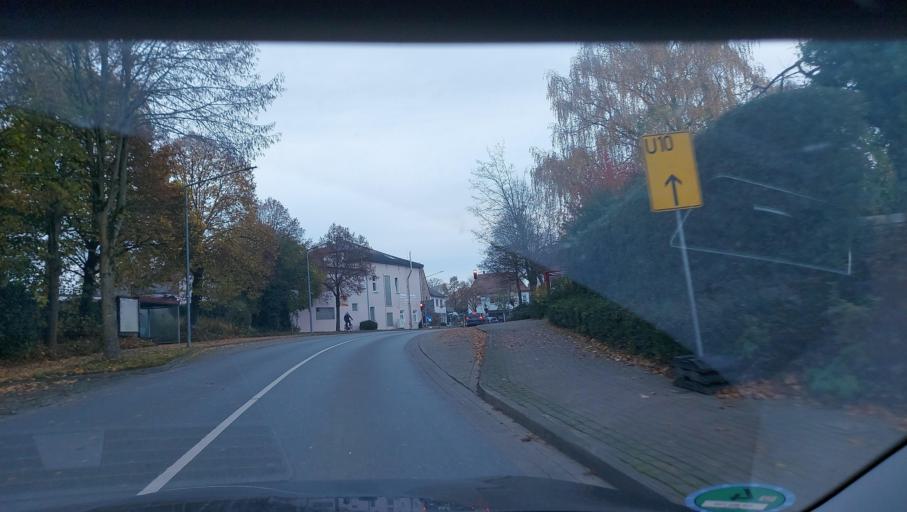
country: DE
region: Lower Saxony
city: Neuenkirchen
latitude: 52.1367
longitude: 8.3894
